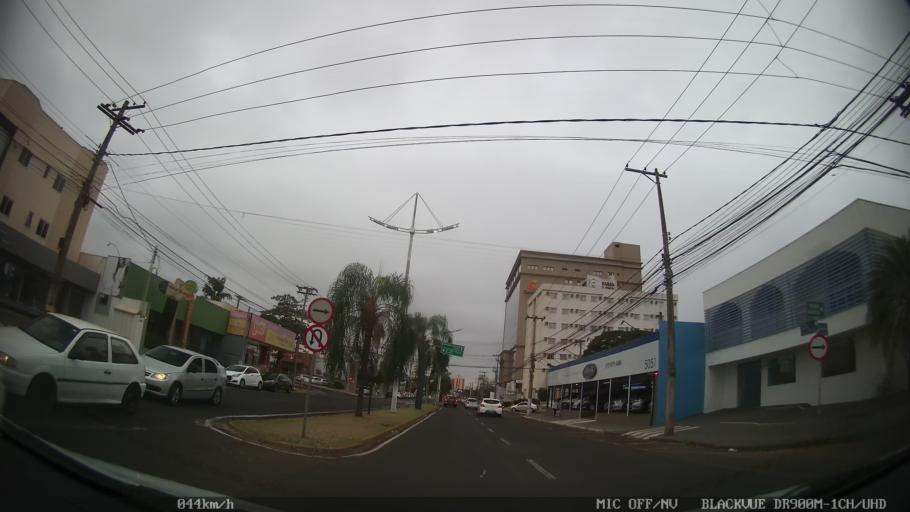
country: BR
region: Sao Paulo
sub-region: Sao Jose Do Rio Preto
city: Sao Jose do Rio Preto
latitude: -20.8251
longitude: -49.3942
